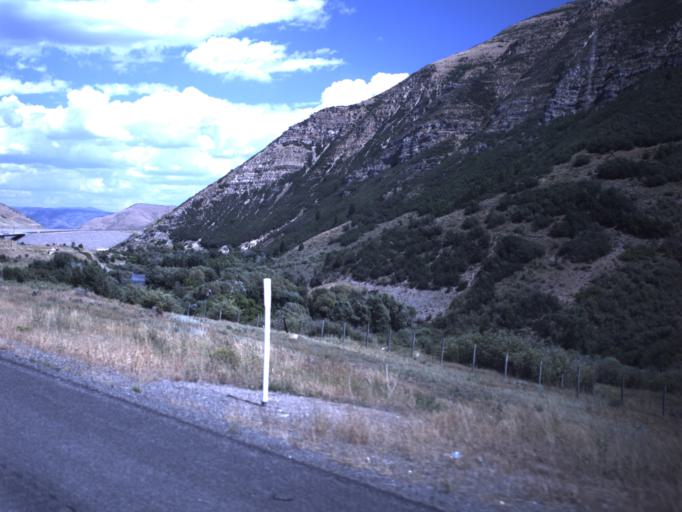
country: US
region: Utah
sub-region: Wasatch County
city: Midway
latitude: 40.3937
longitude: -111.5413
